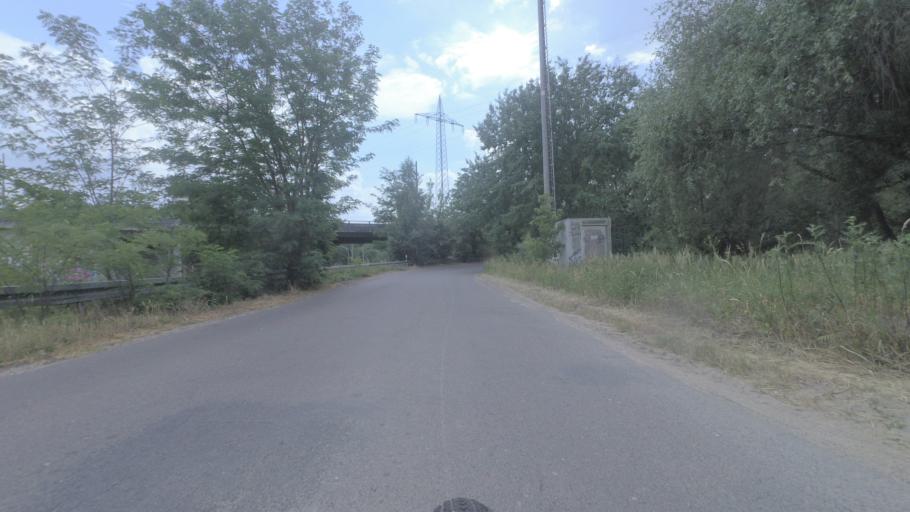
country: DE
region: Brandenburg
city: Ludwigsfelde
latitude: 52.3346
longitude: 13.2775
